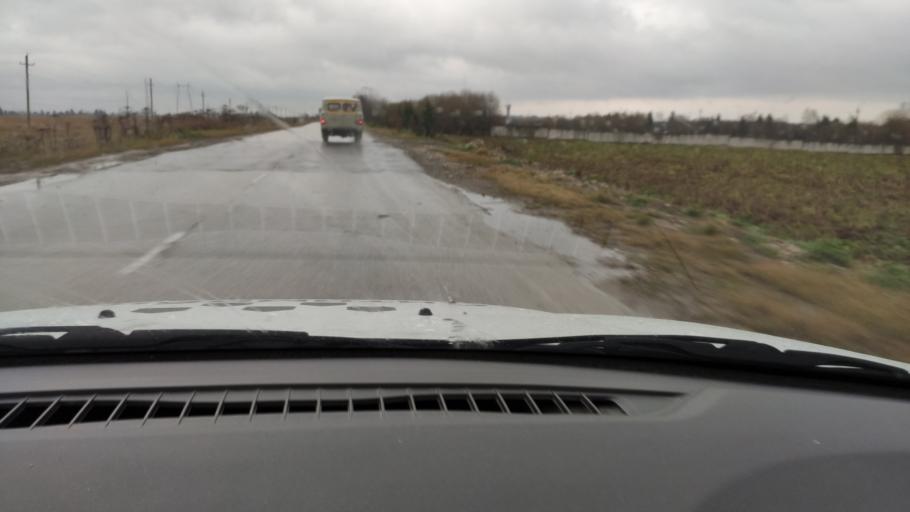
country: RU
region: Perm
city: Sylva
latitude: 58.0292
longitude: 56.6998
